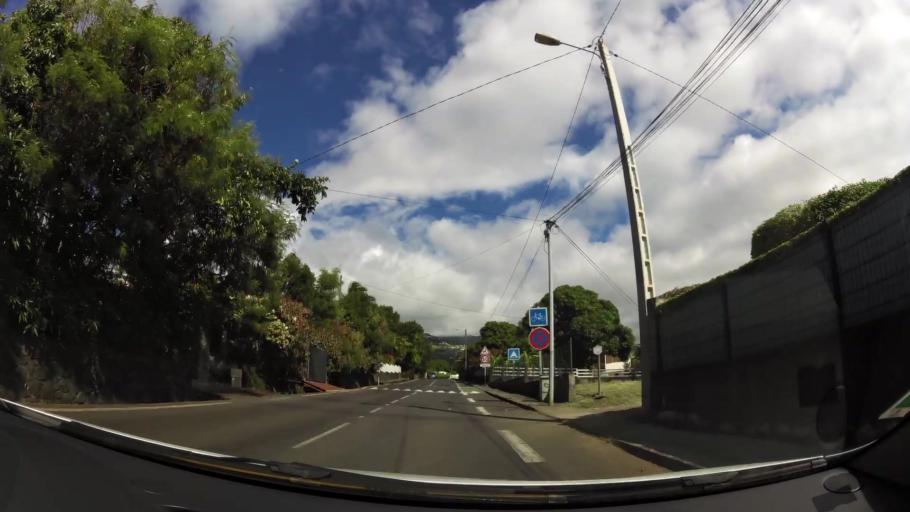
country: RE
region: Reunion
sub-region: Reunion
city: Sainte-Marie
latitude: -20.9135
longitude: 55.4970
